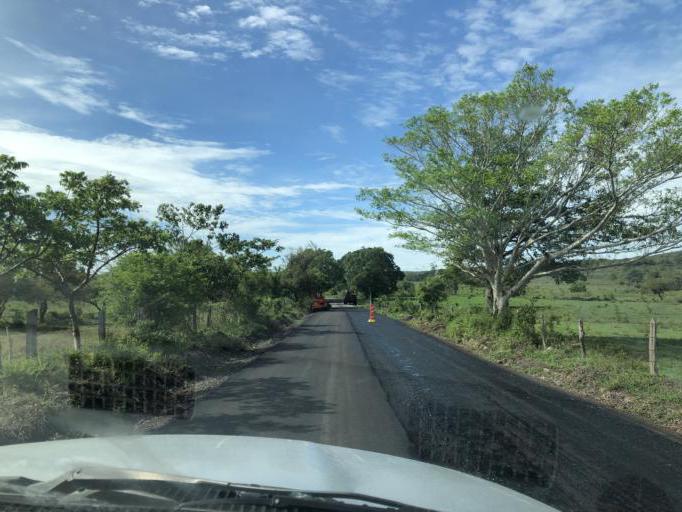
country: MX
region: Veracruz
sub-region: Alto Lucero de Gutierrez Barrios
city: Palma Sola
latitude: 19.8073
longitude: -96.5439
